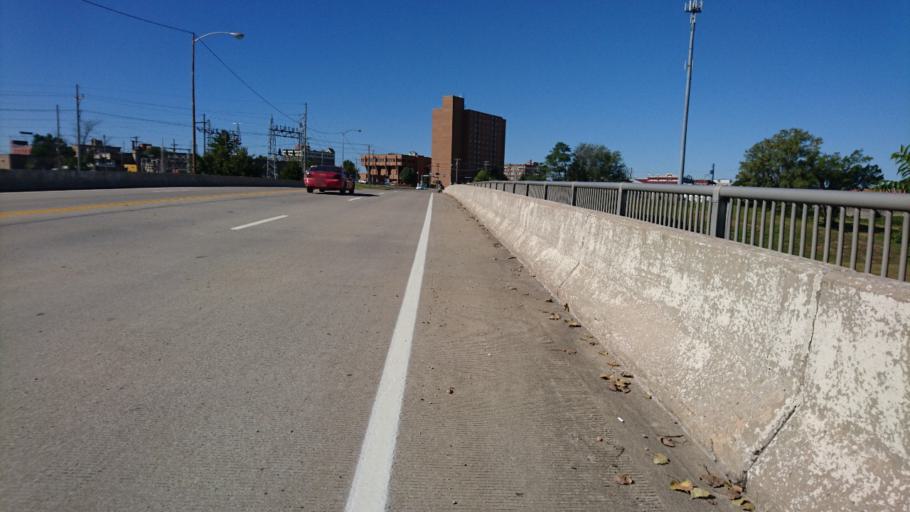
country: US
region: Missouri
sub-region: Jasper County
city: Joplin
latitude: 37.0909
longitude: -94.5099
